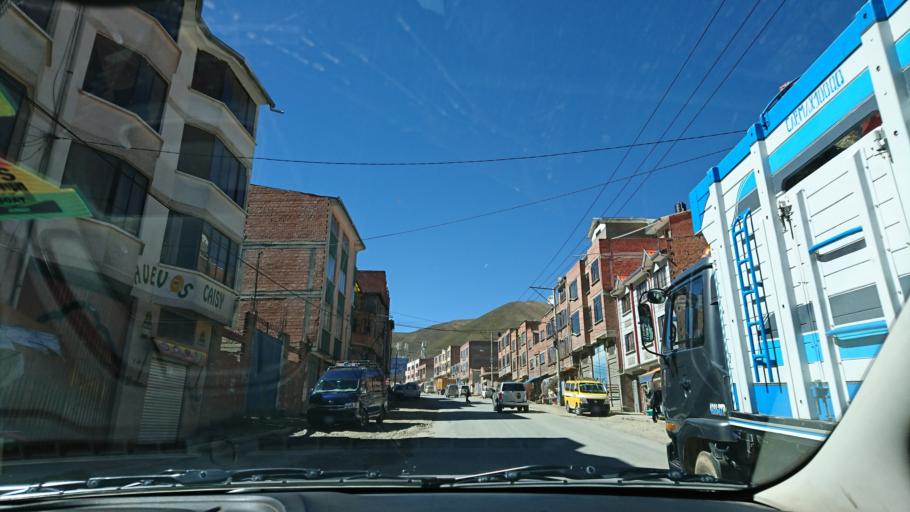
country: BO
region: La Paz
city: La Paz
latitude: -16.4523
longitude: -68.0934
